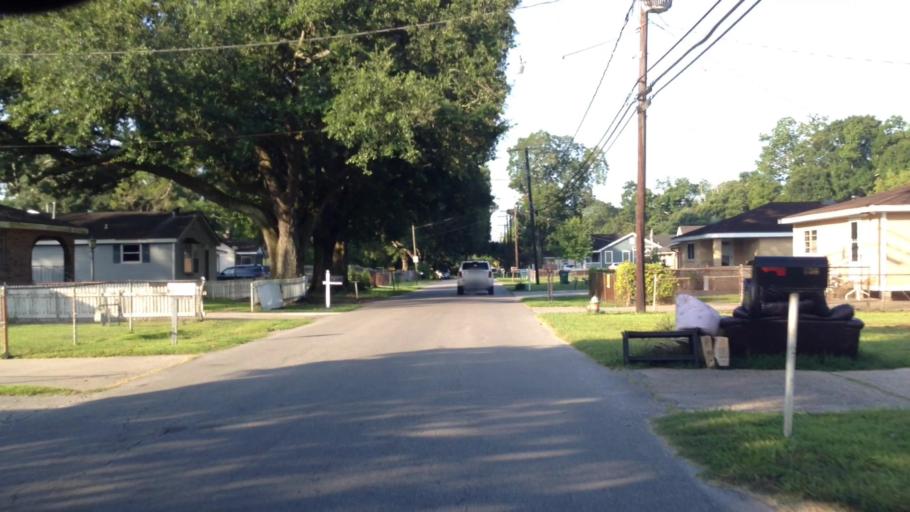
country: US
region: Louisiana
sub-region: Jefferson Parish
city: Bridge City
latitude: 29.9362
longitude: -90.1571
